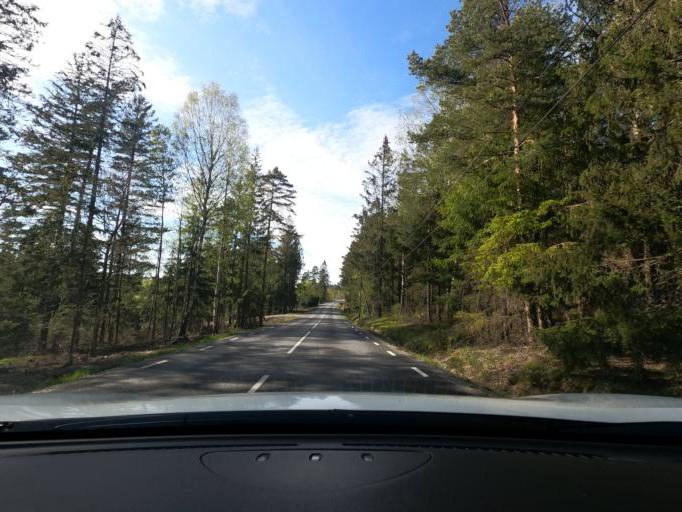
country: SE
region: Vaestra Goetaland
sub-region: Harryda Kommun
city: Landvetter
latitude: 57.6413
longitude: 12.2571
